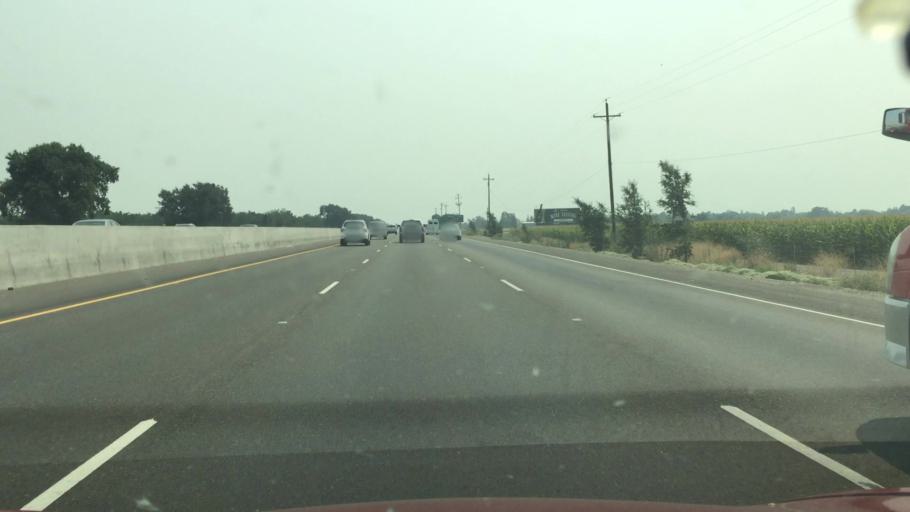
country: US
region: California
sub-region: San Joaquin County
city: French Camp
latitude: 37.8774
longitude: -121.2199
